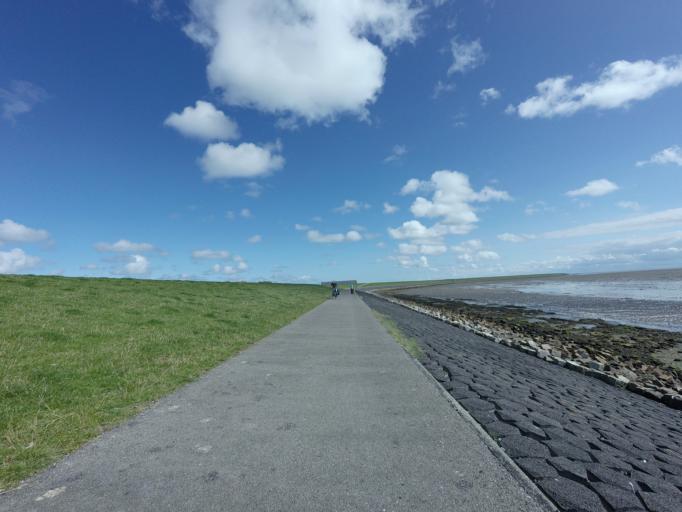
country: NL
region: Friesland
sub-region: Gemeente Terschelling
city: West-Terschelling
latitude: 53.3728
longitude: 5.2723
